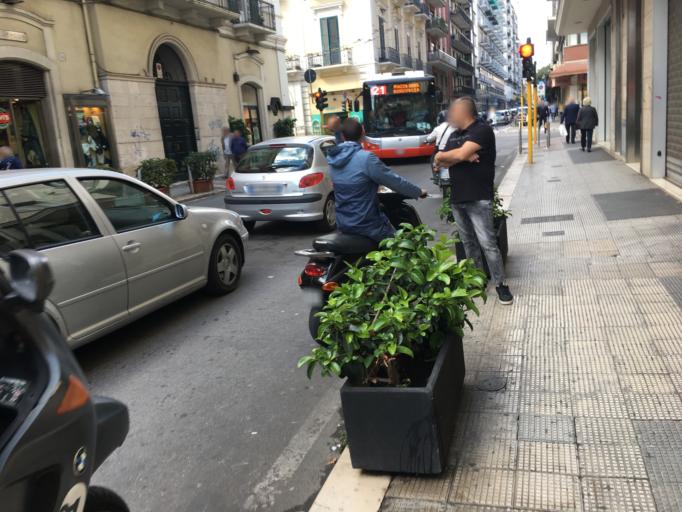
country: IT
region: Apulia
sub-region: Provincia di Bari
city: Bari
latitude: 41.1201
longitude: 16.8723
